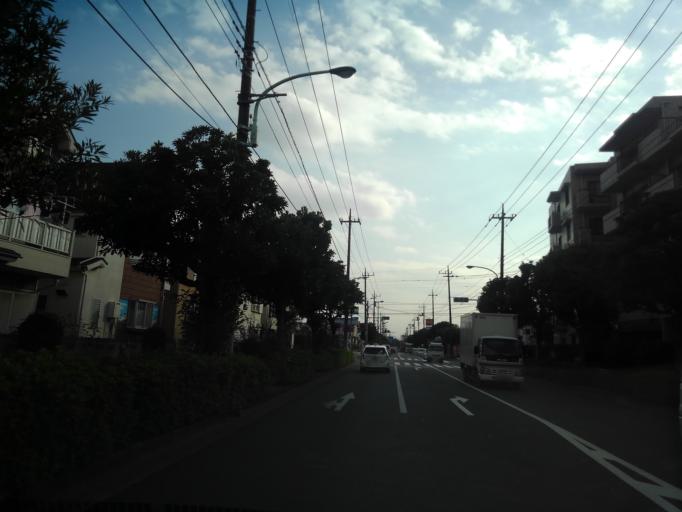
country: JP
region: Tokyo
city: Kokubunji
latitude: 35.7165
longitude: 139.4970
